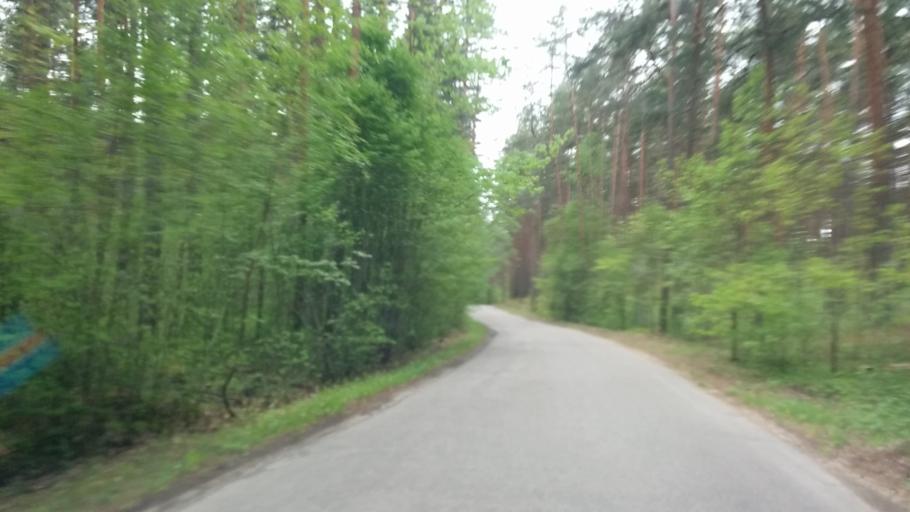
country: LV
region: Babite
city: Pinki
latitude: 56.9430
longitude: 23.9422
